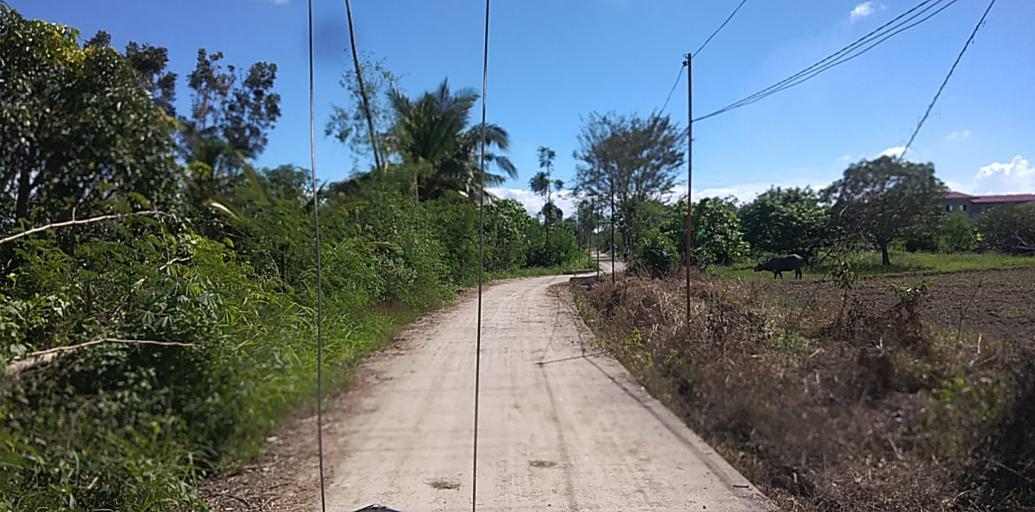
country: PH
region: Central Luzon
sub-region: Province of Pampanga
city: Arayat
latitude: 15.1271
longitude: 120.7872
